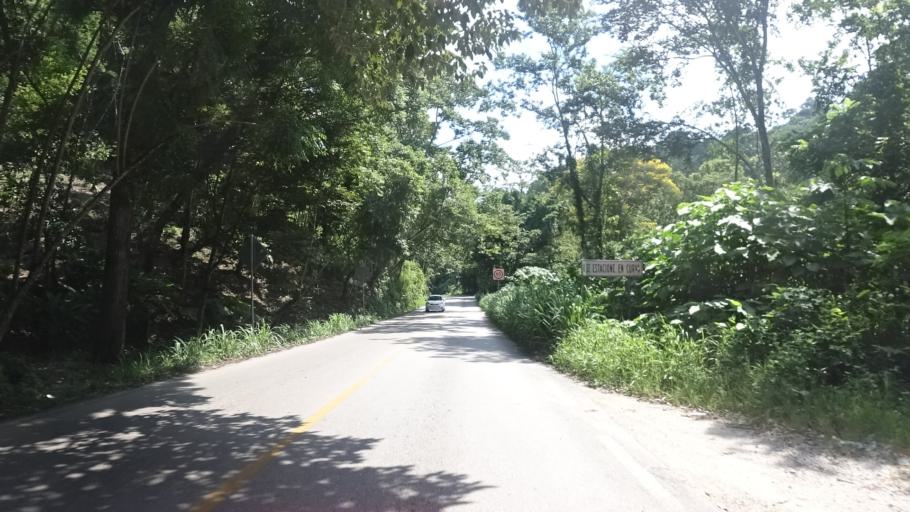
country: MX
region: Chiapas
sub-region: Palenque
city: Doctor Samuel Leon Brindis
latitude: 17.4625
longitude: -91.9643
